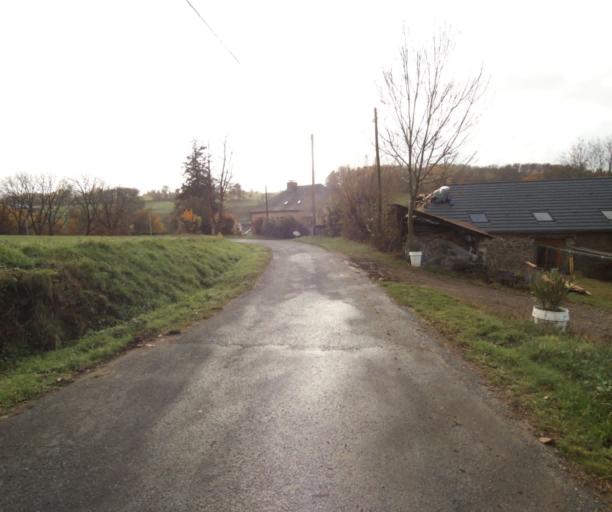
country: FR
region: Limousin
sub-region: Departement de la Correze
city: Sainte-Fereole
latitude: 45.2047
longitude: 1.6338
